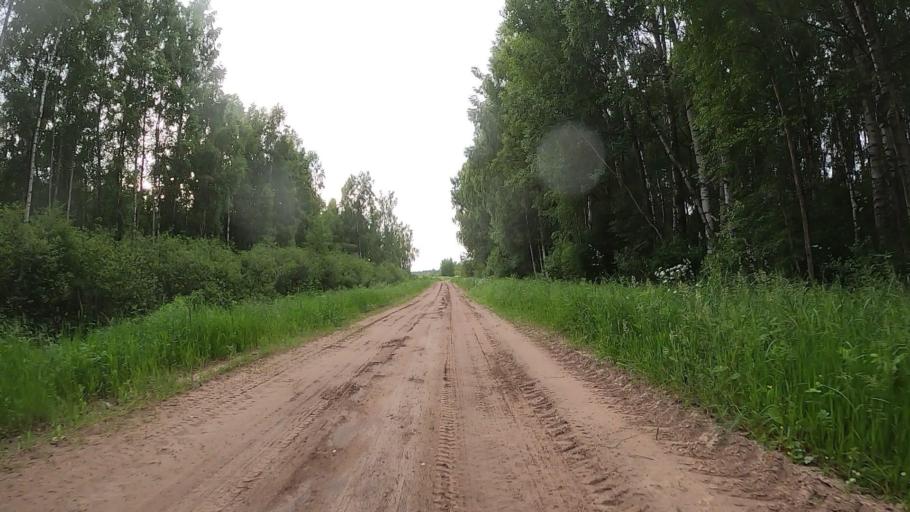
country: LV
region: Olaine
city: Olaine
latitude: 56.8224
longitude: 23.9710
